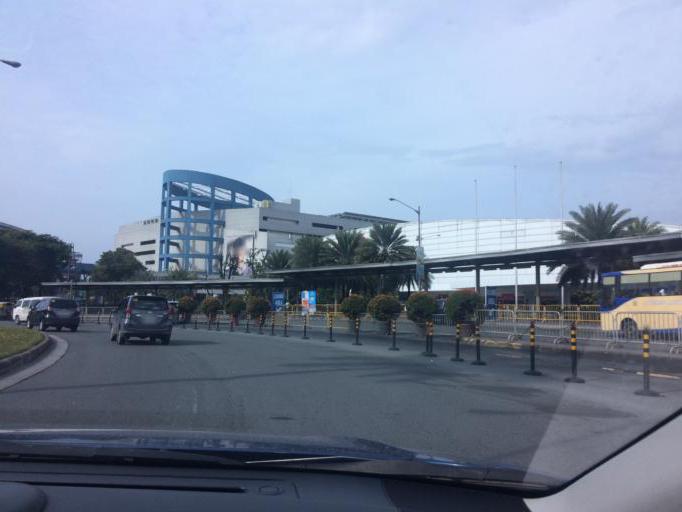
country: PH
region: Metro Manila
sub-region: City of Manila
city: Port Area
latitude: 14.5356
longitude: 120.9837
